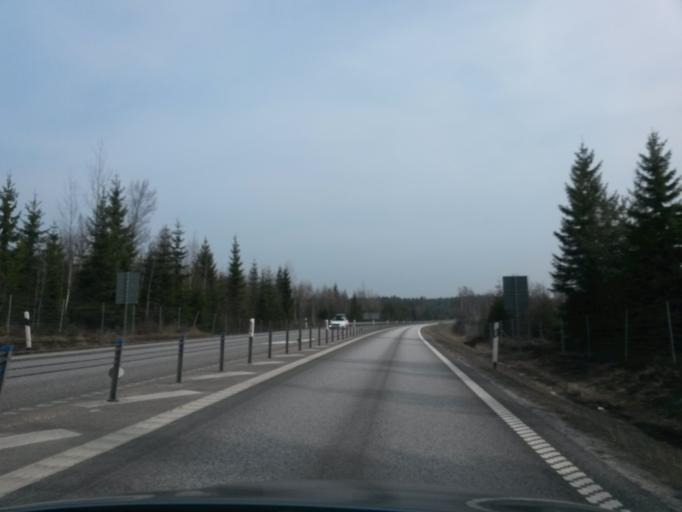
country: SE
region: Vaestra Goetaland
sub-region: Gullspangs Kommun
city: Anderstorp
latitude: 58.9034
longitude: 14.3431
